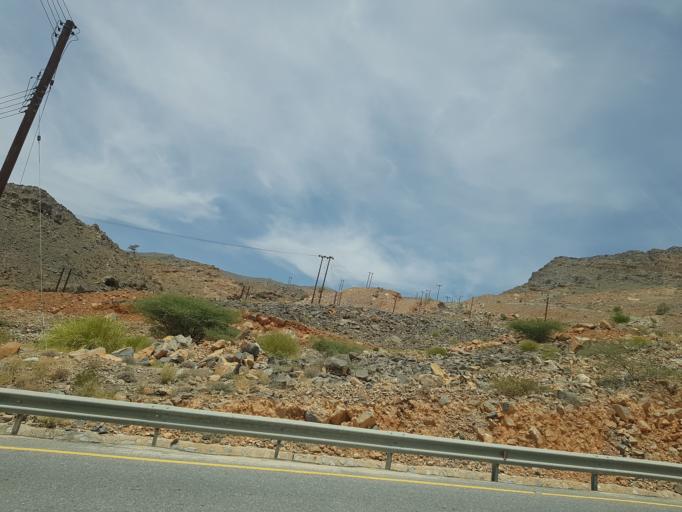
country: OM
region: Muhafazat ad Dakhiliyah
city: Izki
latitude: 22.9791
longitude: 57.7007
